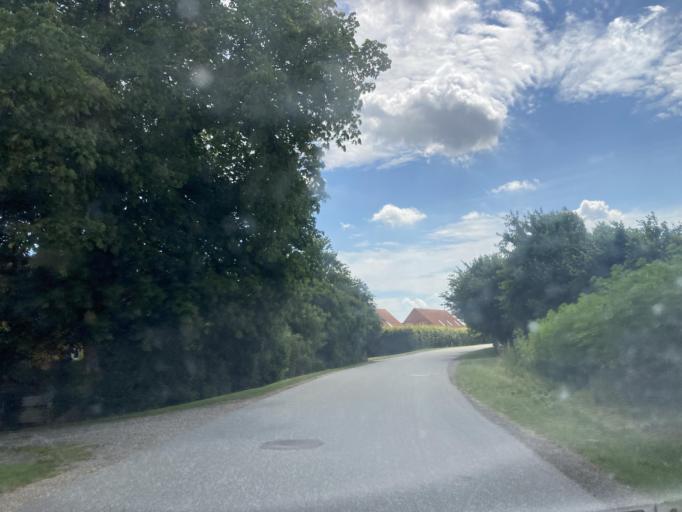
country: DK
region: Zealand
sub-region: Koge Kommune
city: Borup
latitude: 55.4487
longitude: 11.9520
